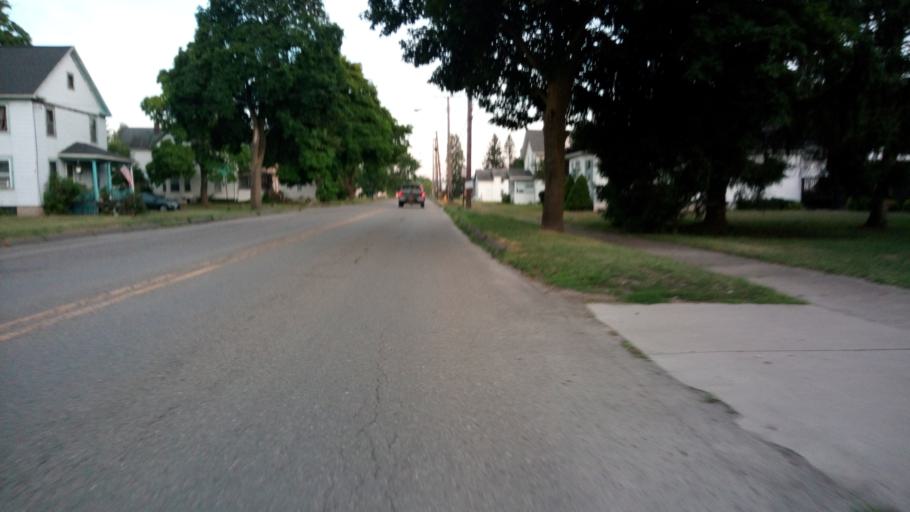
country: US
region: New York
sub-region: Chemung County
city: Elmira Heights
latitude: 42.1242
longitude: -76.8167
